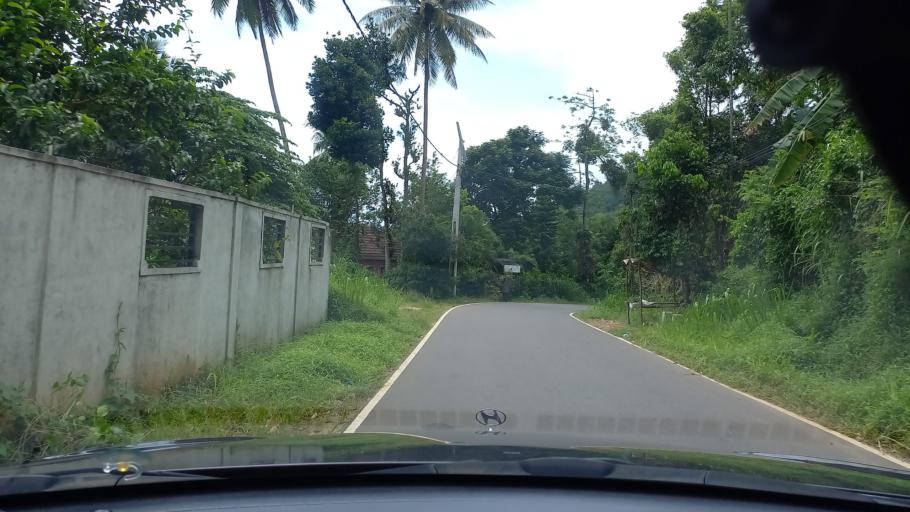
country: LK
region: Central
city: Gampola
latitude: 7.2180
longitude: 80.6101
